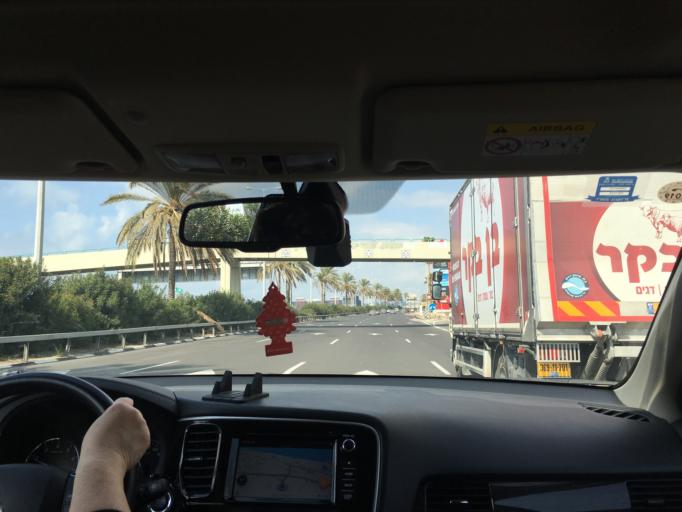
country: IL
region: Tel Aviv
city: Herzliya Pituah
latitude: 32.1464
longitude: 34.8034
